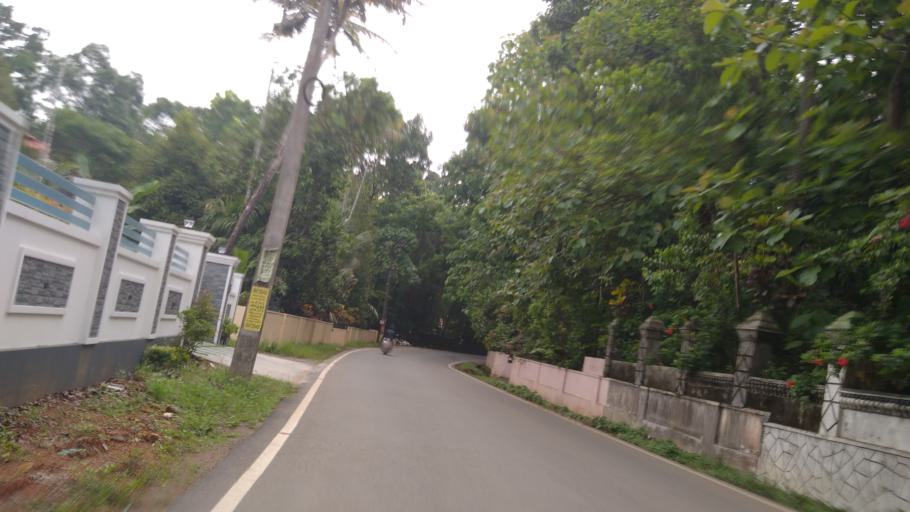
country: IN
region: Kerala
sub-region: Ernakulam
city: Perumpavur
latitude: 10.1227
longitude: 76.5504
